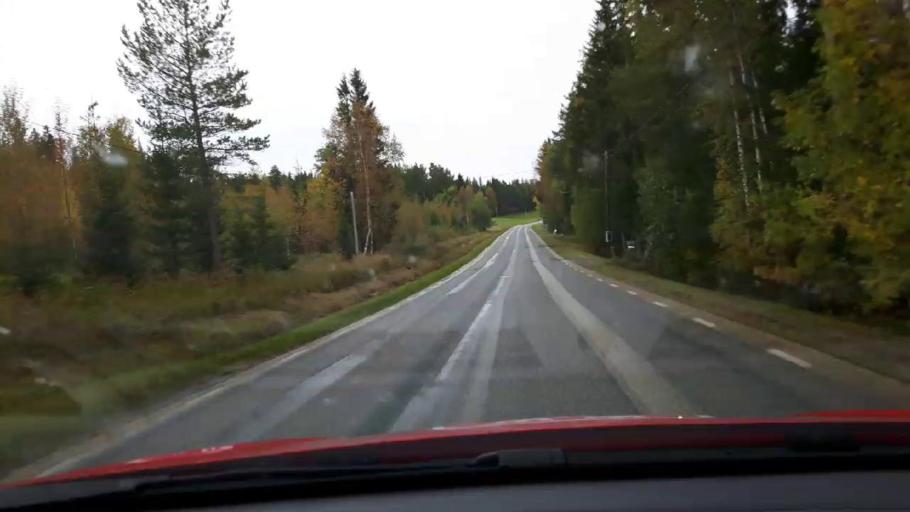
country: SE
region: Jaemtland
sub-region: Bergs Kommun
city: Hoverberg
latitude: 62.8734
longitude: 14.3686
